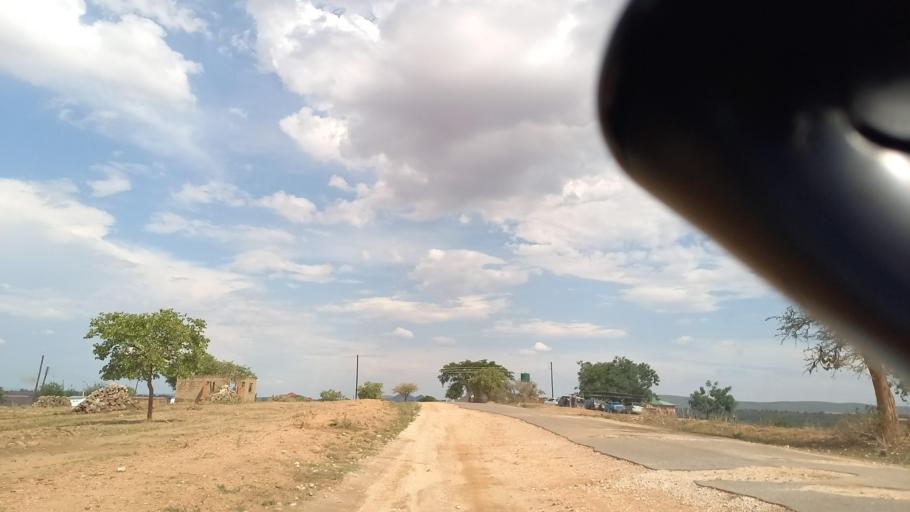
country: ZM
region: Lusaka
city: Kafue
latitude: -16.2170
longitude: 28.1155
